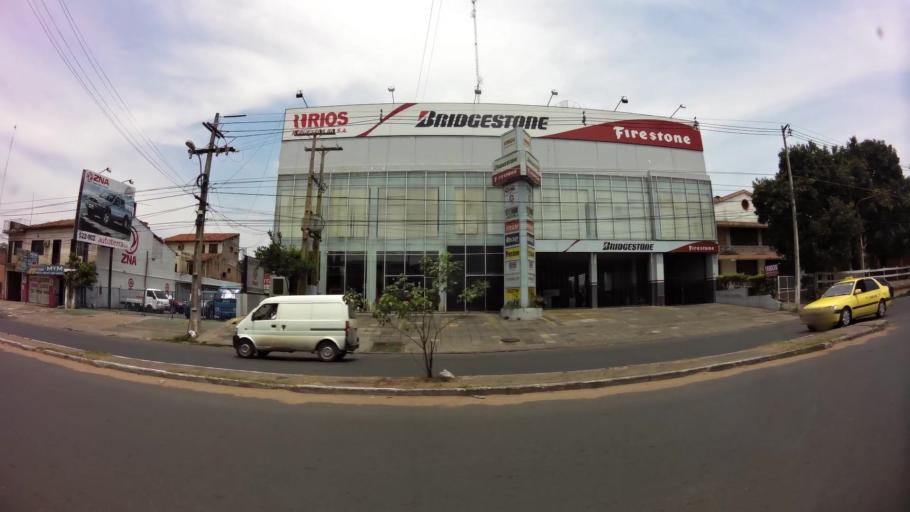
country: PY
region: Central
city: Fernando de la Mora
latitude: -25.3186
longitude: -57.5661
